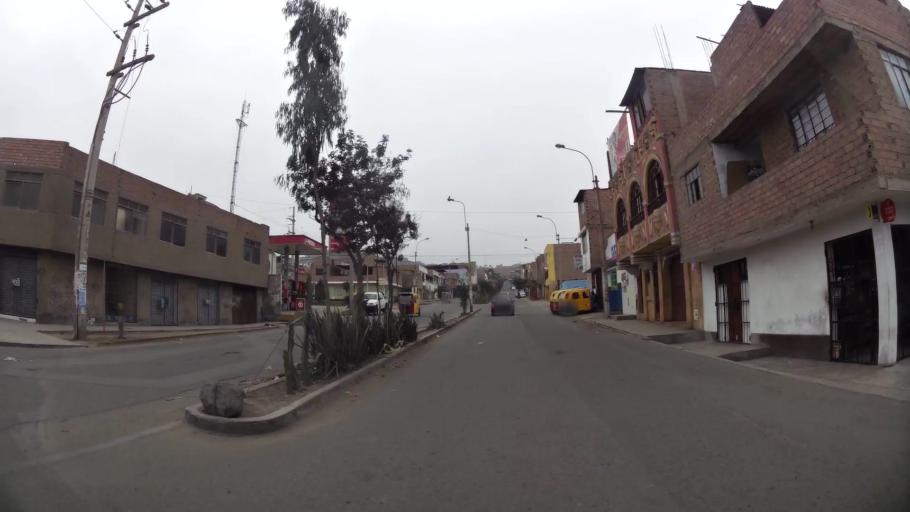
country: PE
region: Lima
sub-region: Lima
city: Surco
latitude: -12.1723
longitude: -76.9655
